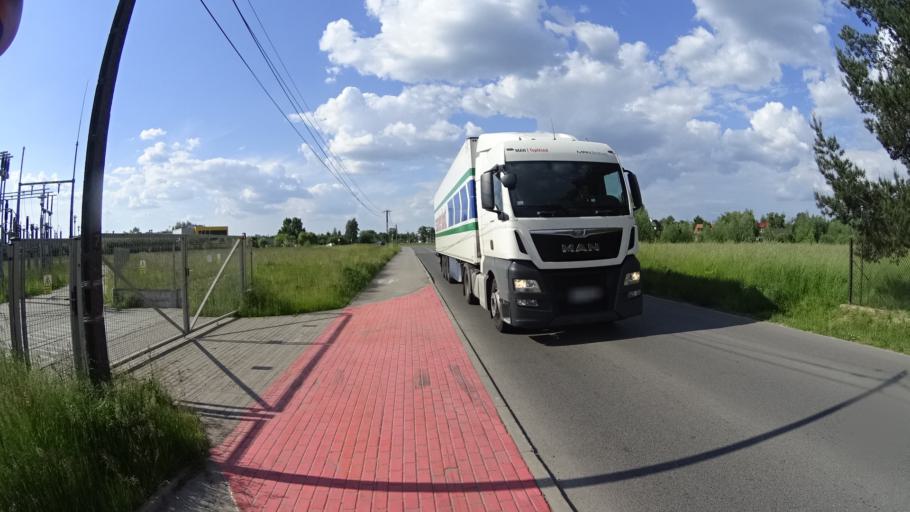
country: PL
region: Masovian Voivodeship
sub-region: Powiat pruszkowski
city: Nadarzyn
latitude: 52.0892
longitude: 20.8153
